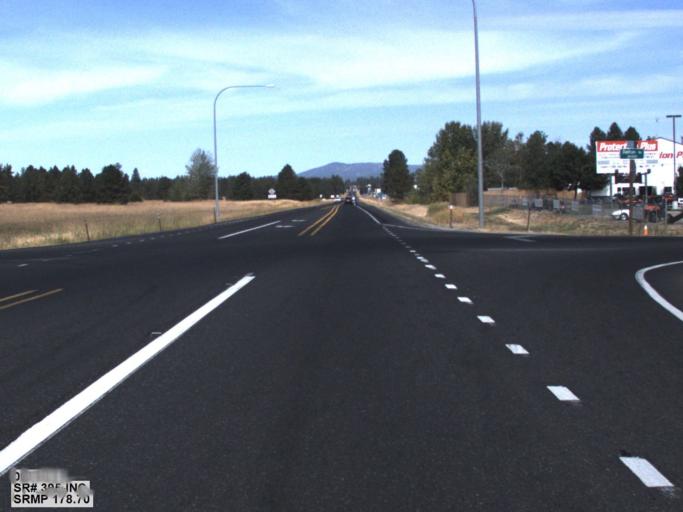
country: US
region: Washington
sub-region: Spokane County
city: Deer Park
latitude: 47.9326
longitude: -117.4676
